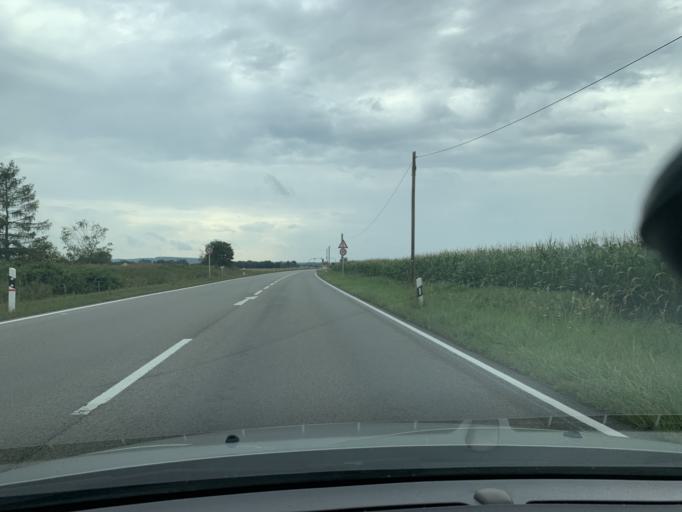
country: DE
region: Bavaria
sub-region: Upper Bavaria
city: Neufahrn
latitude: 48.2502
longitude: 12.4418
